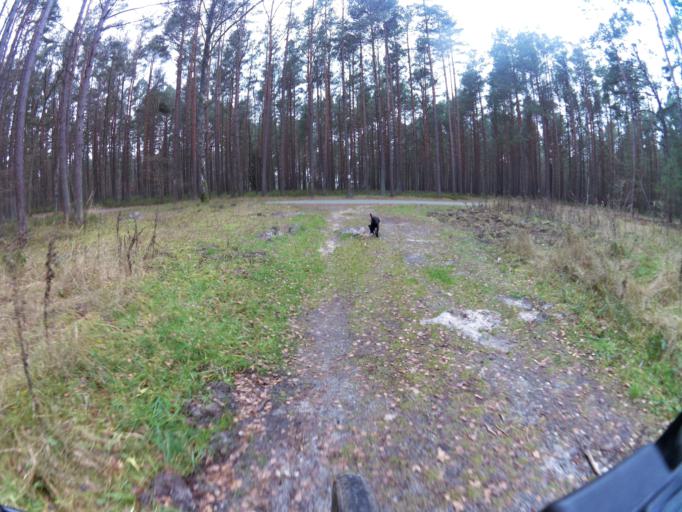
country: PL
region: West Pomeranian Voivodeship
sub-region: Powiat gryficki
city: Cerkwica
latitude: 54.0972
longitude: 15.1293
